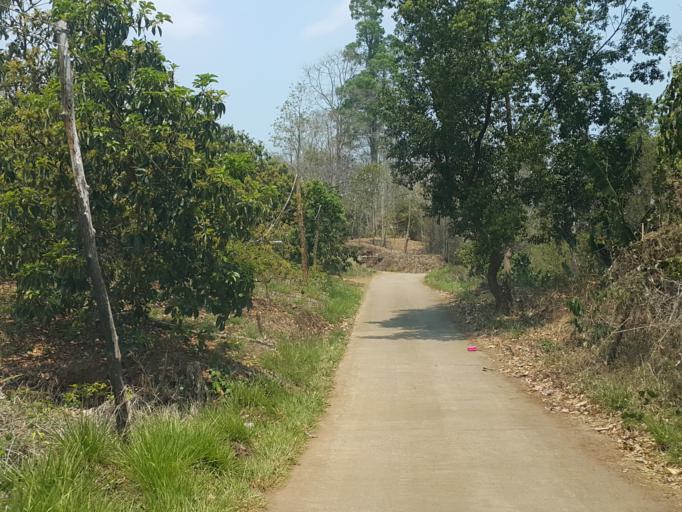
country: TH
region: Chiang Mai
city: Samoeng
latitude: 18.7928
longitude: 98.8087
